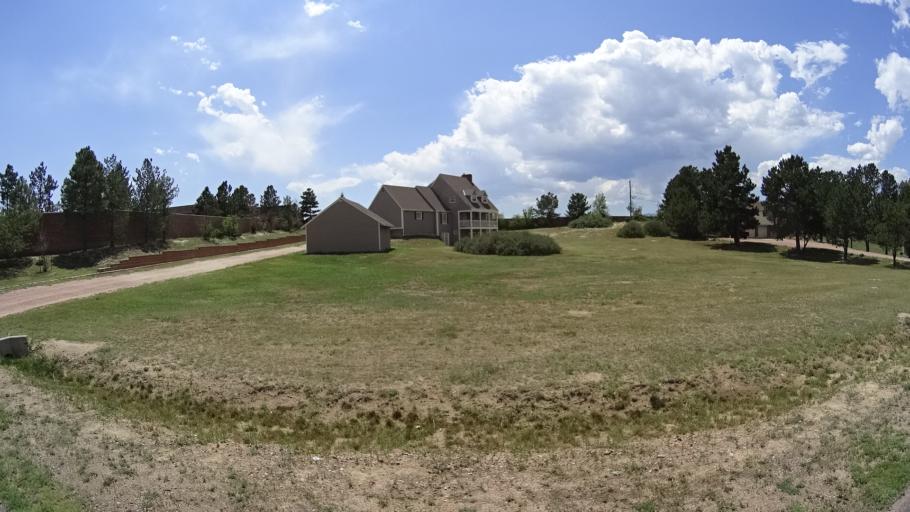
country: US
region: Colorado
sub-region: El Paso County
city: Air Force Academy
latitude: 38.9347
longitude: -104.8016
